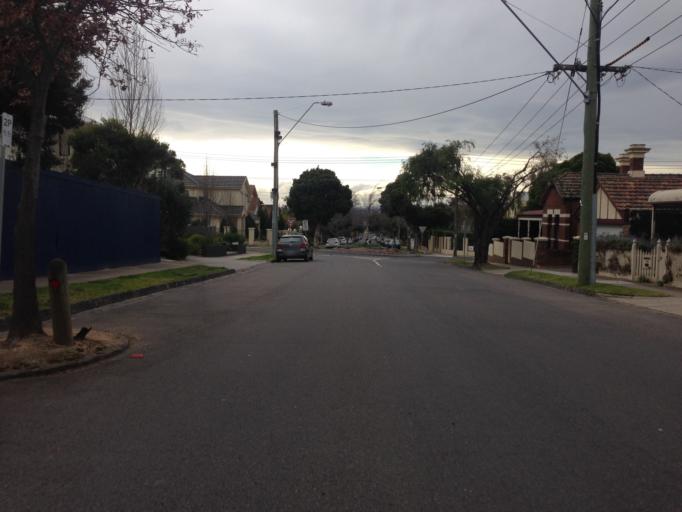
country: AU
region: Victoria
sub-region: Boroondara
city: Kew
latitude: -37.8004
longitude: 145.0352
